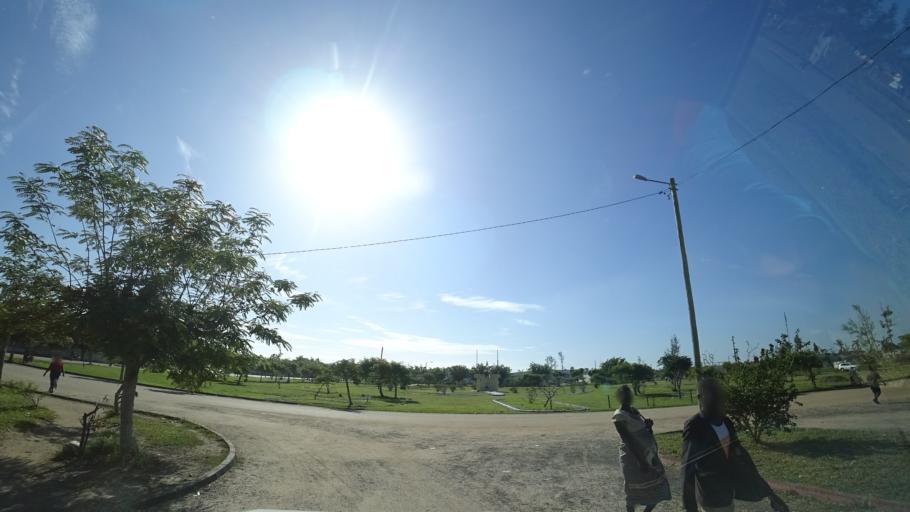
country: MZ
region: Sofala
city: Dondo
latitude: -19.6171
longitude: 34.7416
